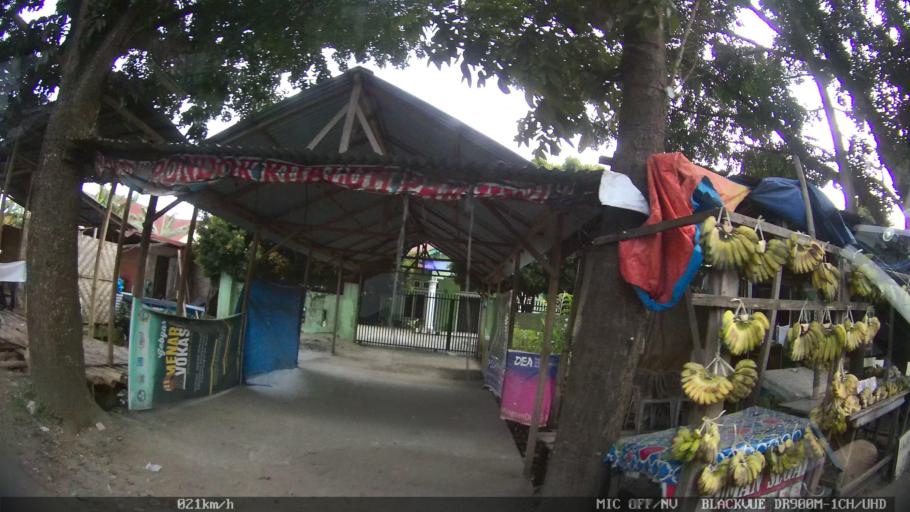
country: ID
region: North Sumatra
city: Medan
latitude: 3.5813
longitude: 98.7431
